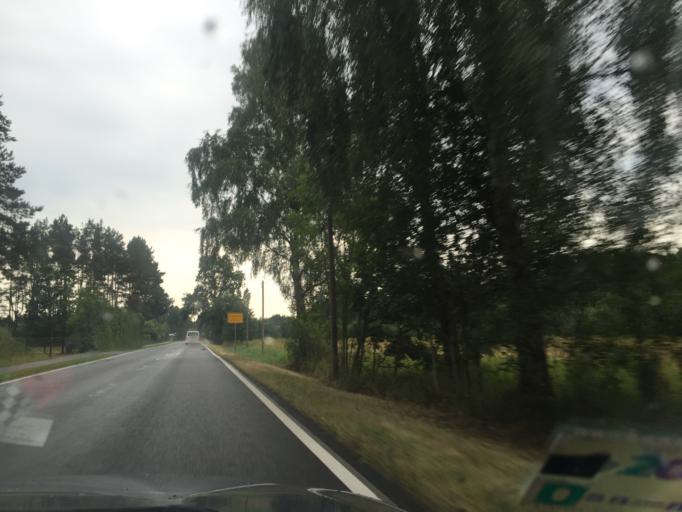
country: DE
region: Brandenburg
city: Liebenwalde
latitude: 52.8390
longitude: 13.4067
